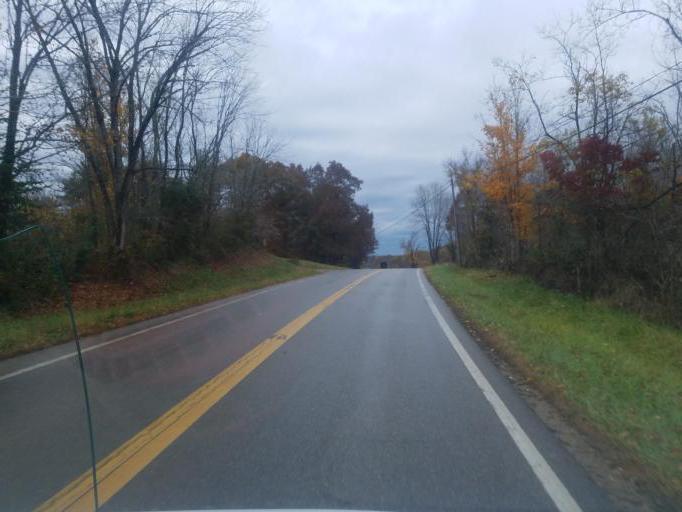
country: US
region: Ohio
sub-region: Morgan County
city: McConnelsville
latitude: 39.5156
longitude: -81.8505
